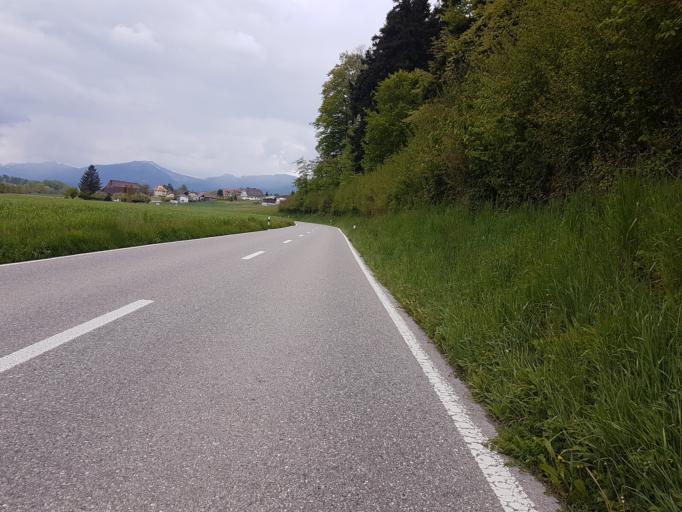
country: CH
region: Bern
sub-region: Oberaargau
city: Niederbipp
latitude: 47.2341
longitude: 7.7015
